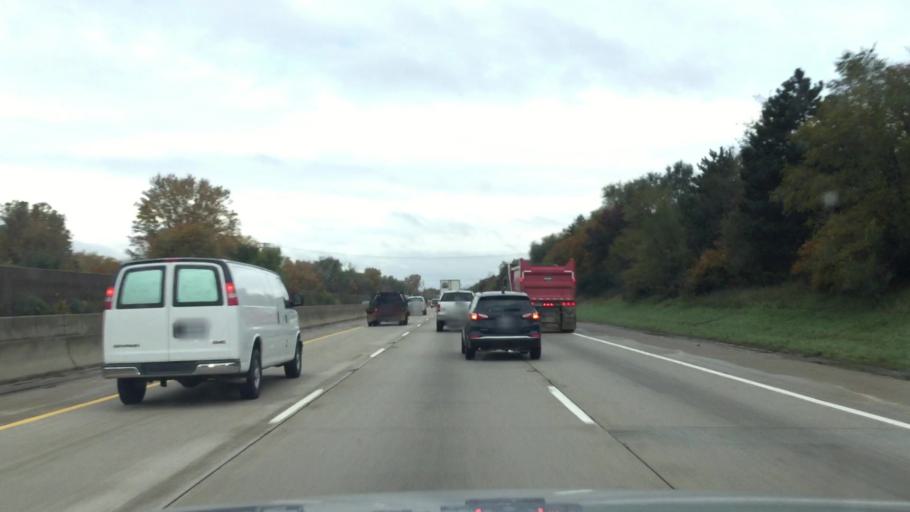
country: US
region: Michigan
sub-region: Washtenaw County
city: Ypsilanti
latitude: 42.2234
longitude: -83.5668
